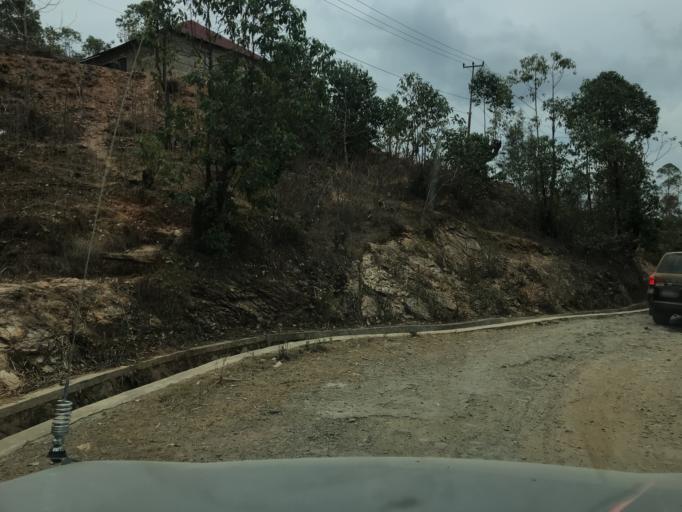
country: TL
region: Ermera
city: Gleno
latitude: -8.8388
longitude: 125.4396
